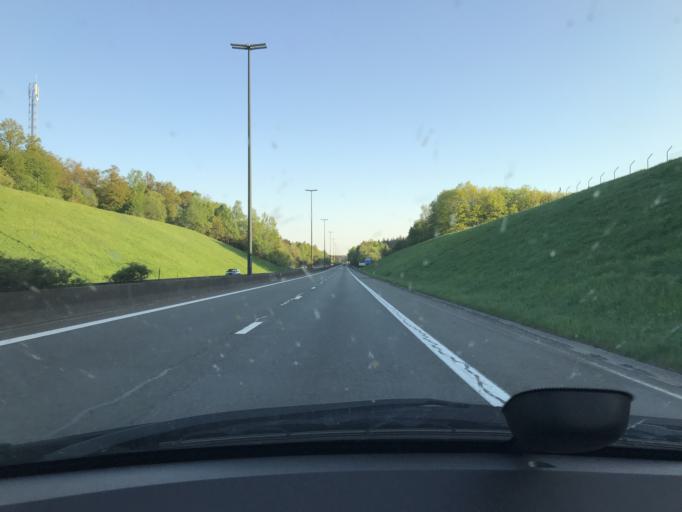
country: BE
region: Wallonia
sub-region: Province du Luxembourg
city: Libin
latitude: 49.9588
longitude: 5.2379
